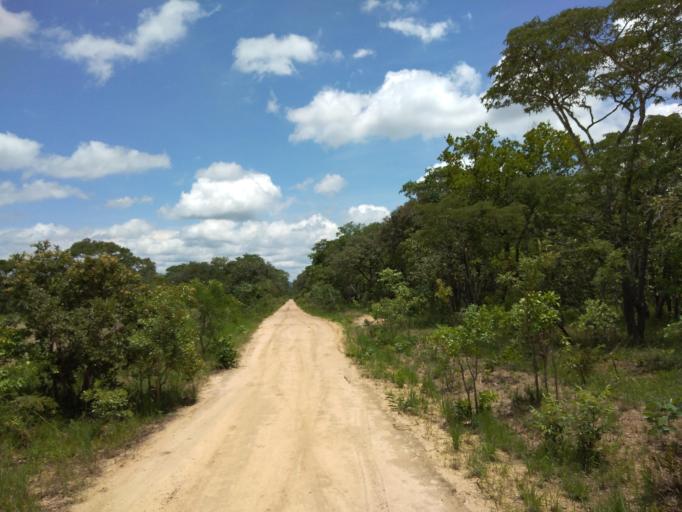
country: ZM
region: Central
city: Mkushi
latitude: -13.9531
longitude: 29.8770
